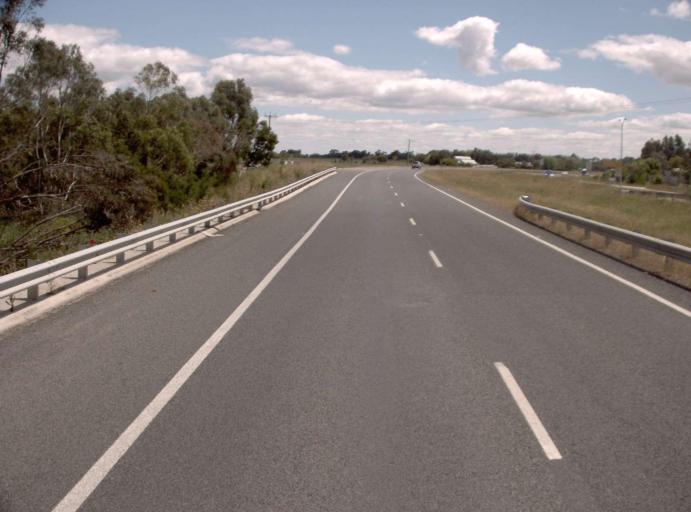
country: AU
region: Victoria
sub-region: Bass Coast
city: North Wonthaggi
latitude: -38.4855
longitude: 145.4643
